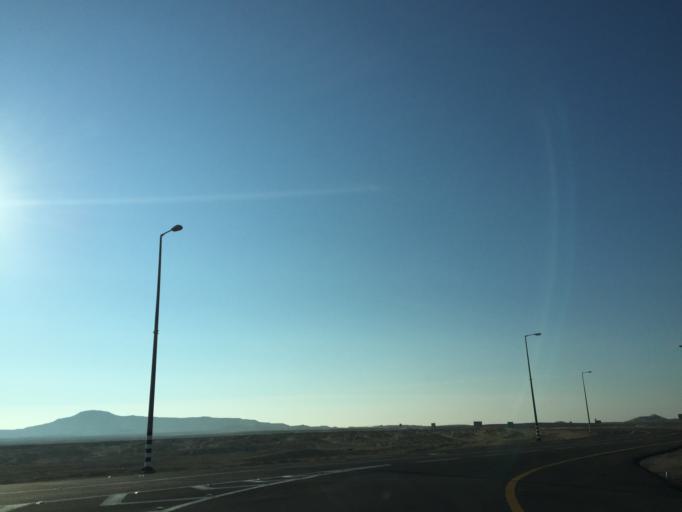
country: IL
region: Southern District
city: Mitzpe Ramon
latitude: 30.2771
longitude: 35.0205
